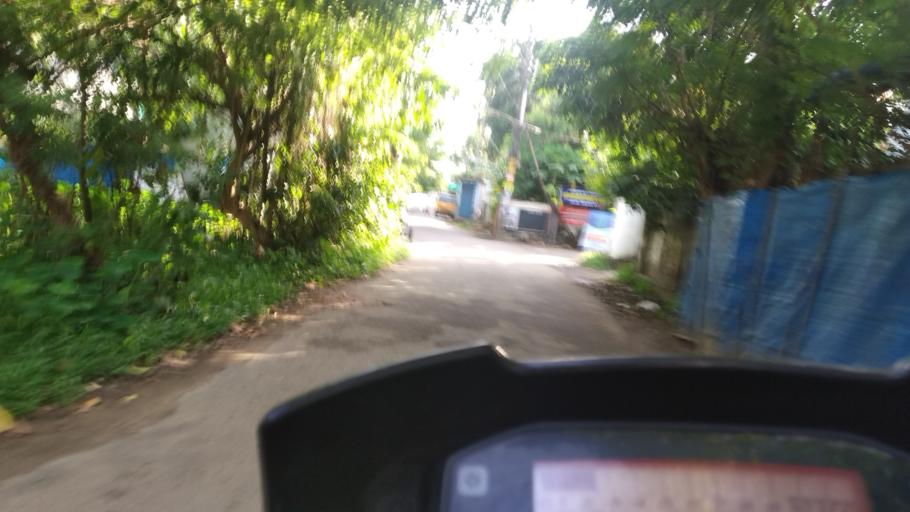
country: IN
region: Kerala
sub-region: Thrissur District
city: Kodungallur
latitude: 10.1343
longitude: 76.1928
